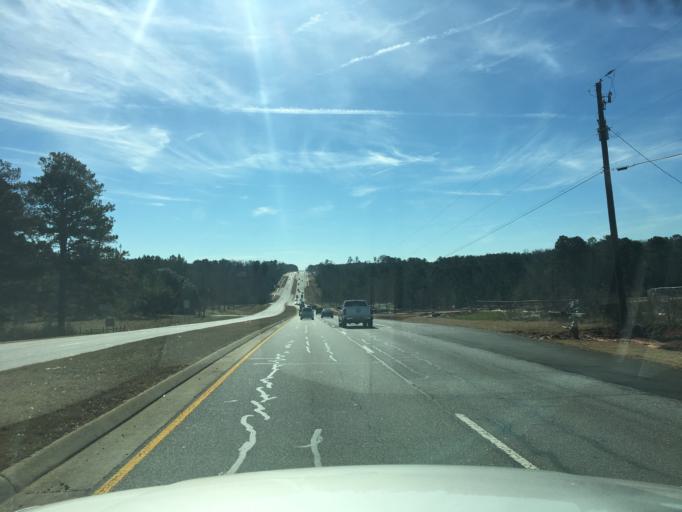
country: US
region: Georgia
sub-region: Gwinnett County
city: Lawrenceville
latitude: 33.9149
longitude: -84.0009
